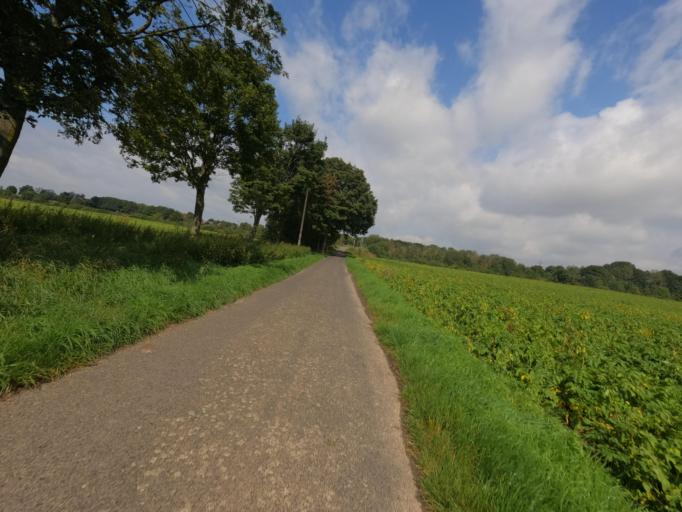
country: DE
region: North Rhine-Westphalia
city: Baesweiler
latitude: 50.9335
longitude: 6.2039
